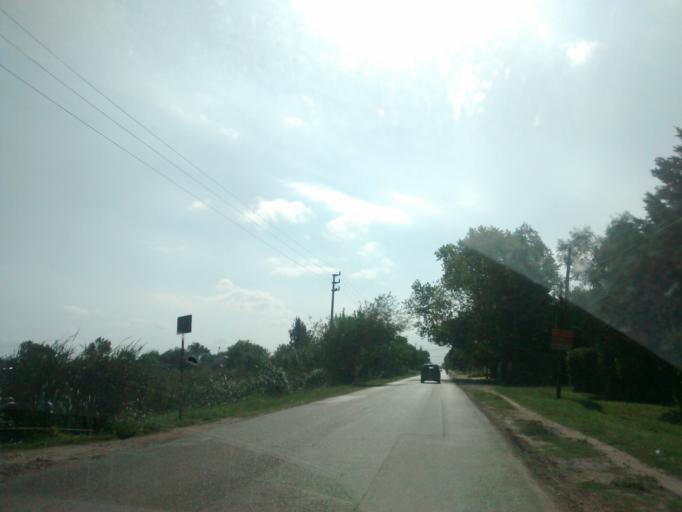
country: AR
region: Buenos Aires
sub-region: Partido de La Plata
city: La Plata
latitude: -34.9727
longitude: -57.8728
